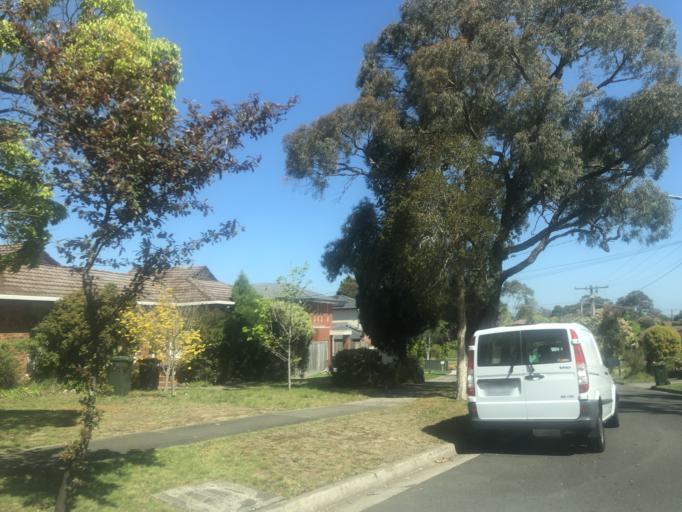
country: AU
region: Victoria
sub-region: Monash
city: Notting Hill
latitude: -37.9022
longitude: 145.1727
